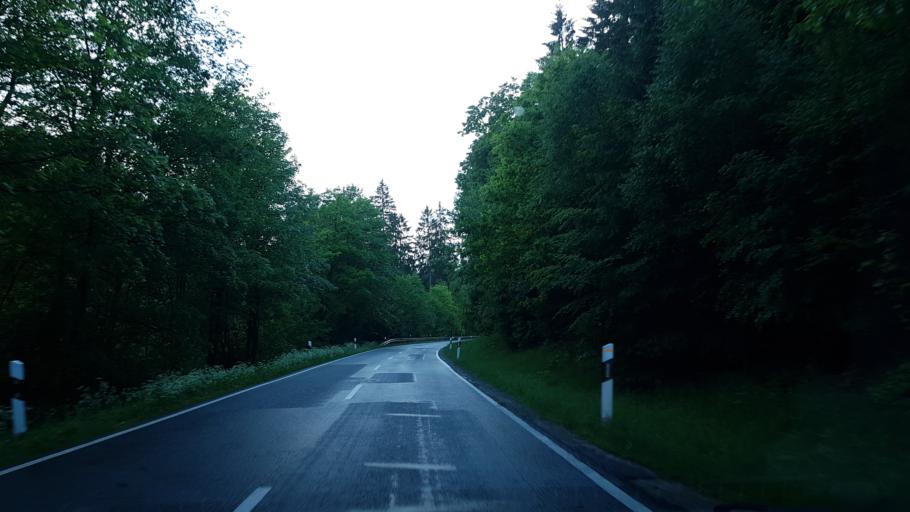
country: DE
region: Lower Saxony
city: Uslar
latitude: 51.7238
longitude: 9.6231
